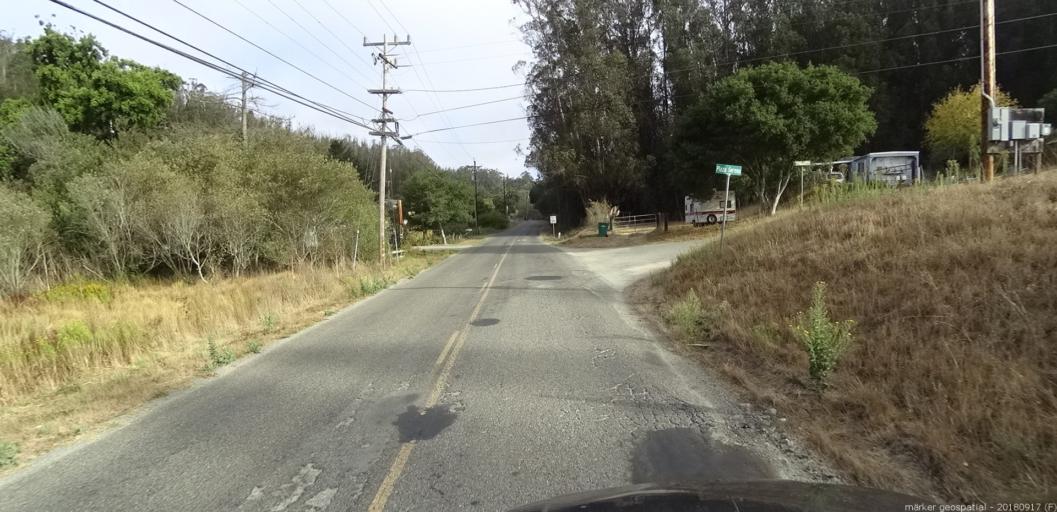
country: US
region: California
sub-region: Monterey County
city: Elkhorn
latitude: 36.8090
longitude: -121.7039
